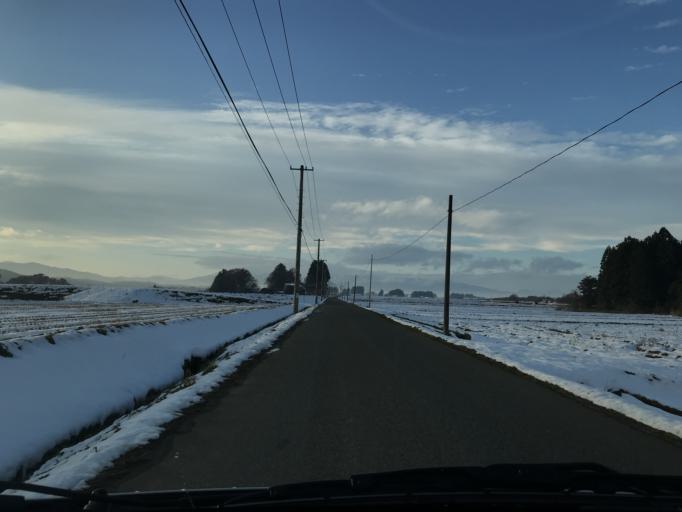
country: JP
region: Iwate
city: Mizusawa
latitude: 39.0483
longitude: 141.1058
